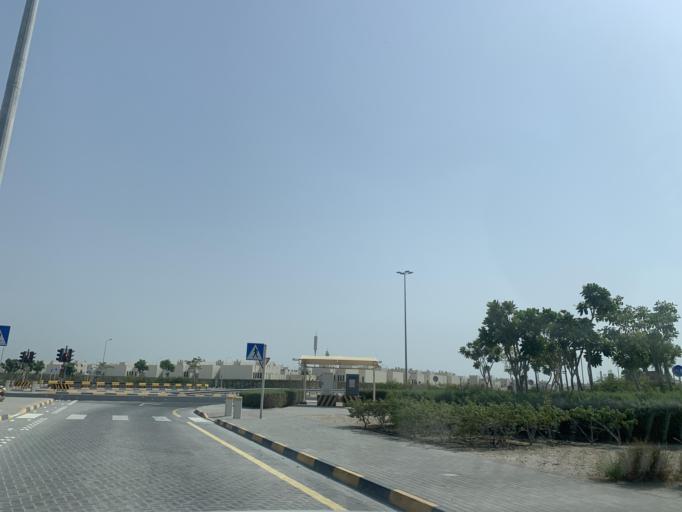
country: BH
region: Muharraq
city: Al Muharraq
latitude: 26.3055
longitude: 50.6395
